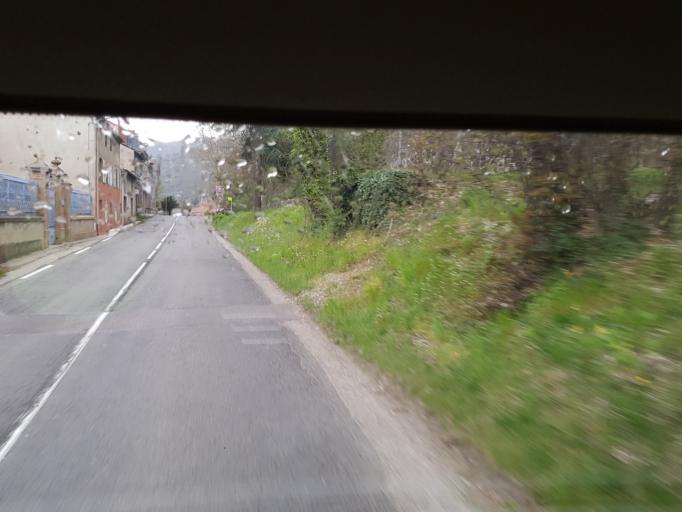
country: FR
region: Rhone-Alpes
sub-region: Departement de la Loire
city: Saint-Paul-en-Cornillon
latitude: 45.4045
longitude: 4.2448
